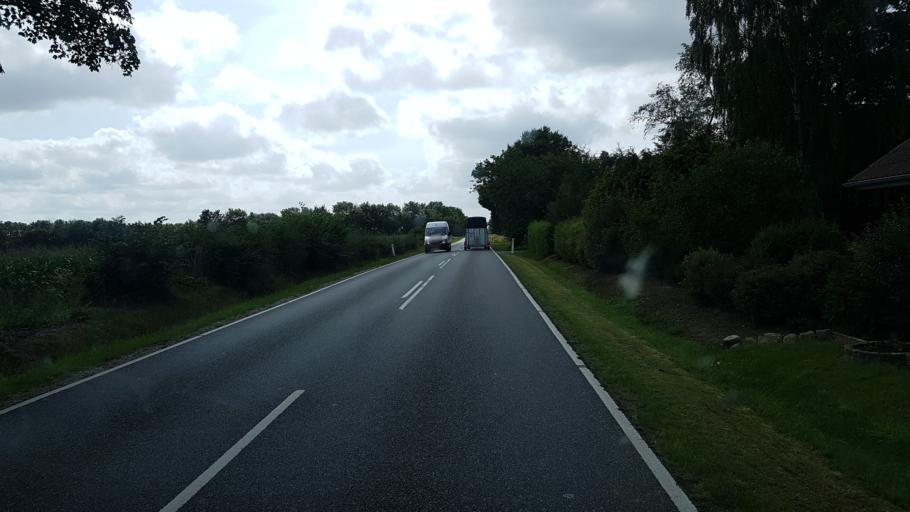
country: DK
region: South Denmark
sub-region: Vejen Kommune
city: Brorup
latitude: 55.5325
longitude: 9.0515
